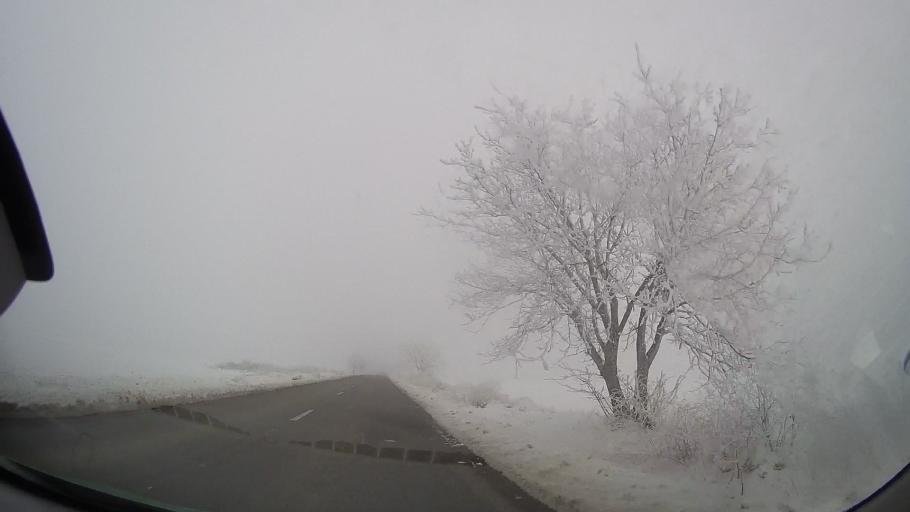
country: RO
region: Iasi
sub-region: Comuna Mogosesti-Siret
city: Mogosesti-Siret
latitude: 47.1506
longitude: 26.7776
